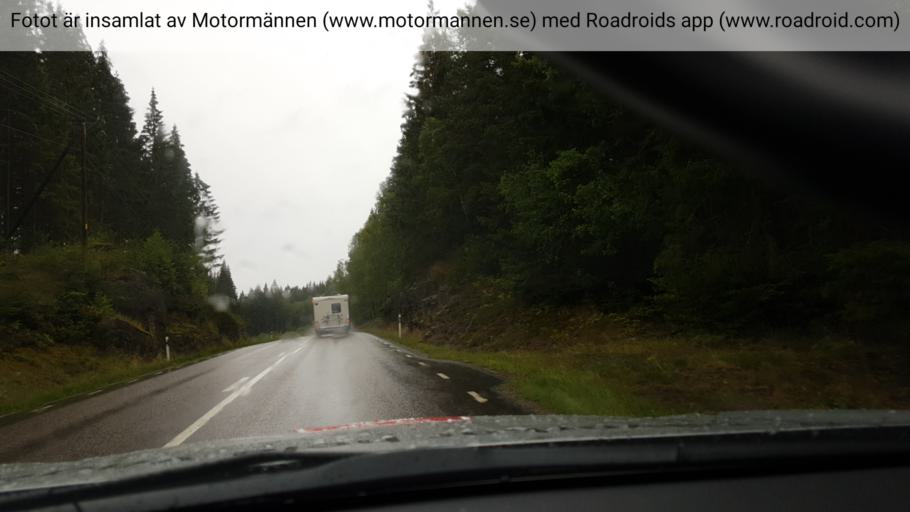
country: SE
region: Vaestra Goetaland
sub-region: Vargarda Kommun
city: Jonstorp
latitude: 58.0822
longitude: 12.6750
